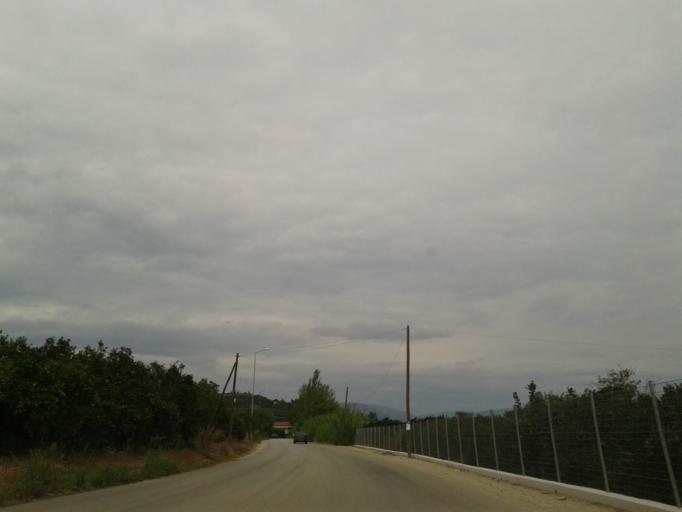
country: GR
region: Peloponnese
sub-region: Nomos Argolidos
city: Argos
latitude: 37.6086
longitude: 22.7009
